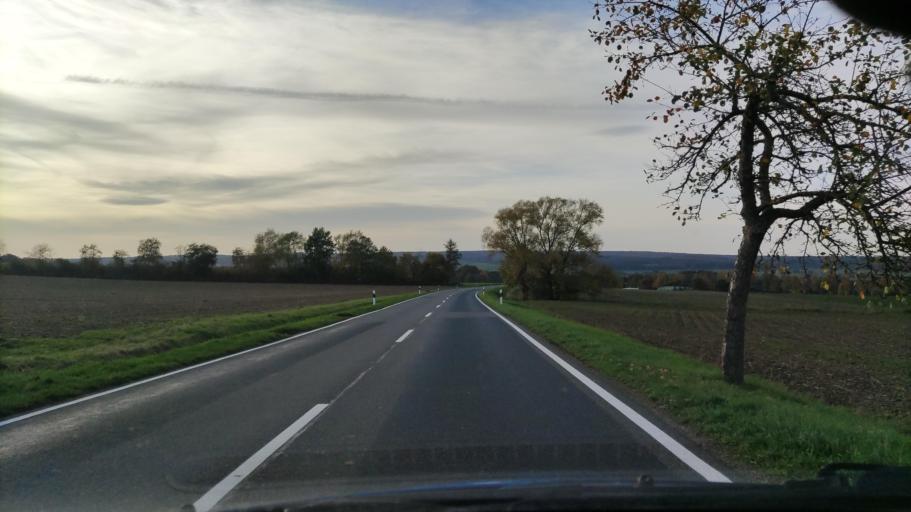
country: DE
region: Lower Saxony
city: Dassel
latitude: 51.7751
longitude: 9.7050
